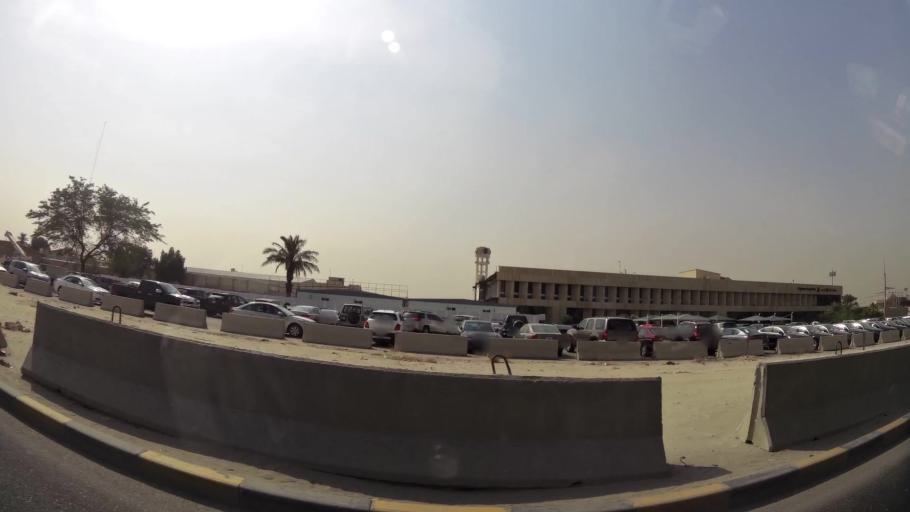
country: KW
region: Al Asimah
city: Ash Shamiyah
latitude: 29.3386
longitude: 47.9475
